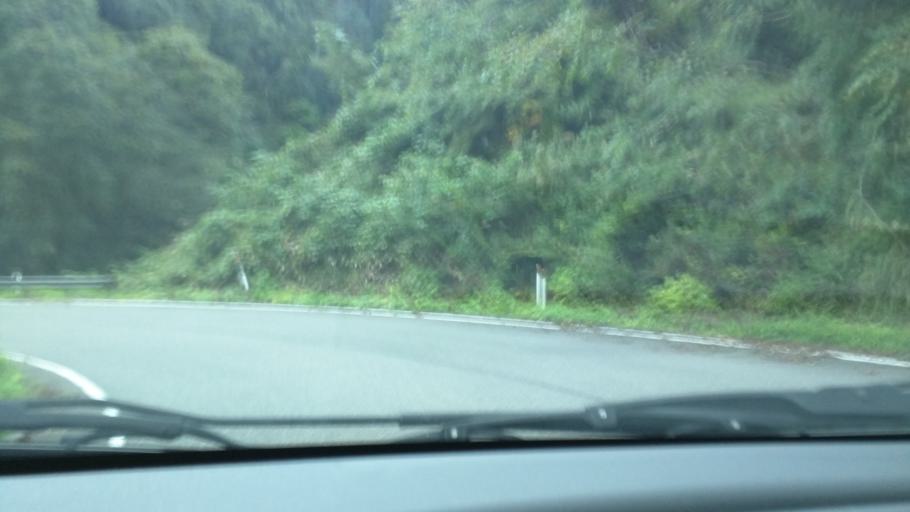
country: JP
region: Fukushima
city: Kitakata
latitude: 37.4578
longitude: 139.7191
